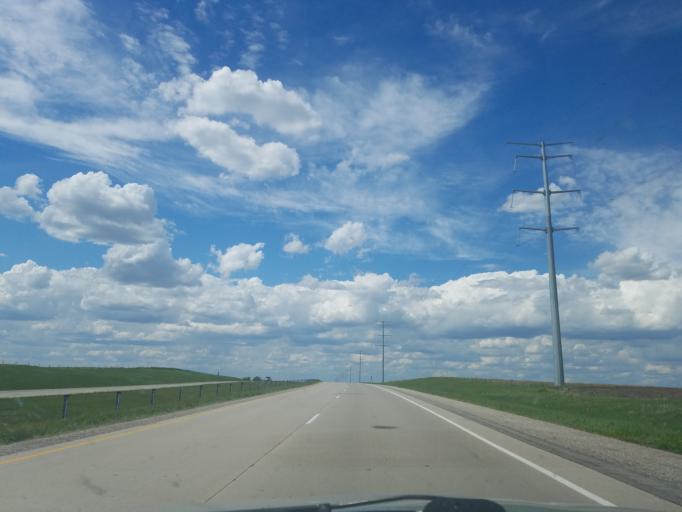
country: US
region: Minnesota
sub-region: Clay County
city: Barnesville
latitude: 46.5255
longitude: -96.2923
